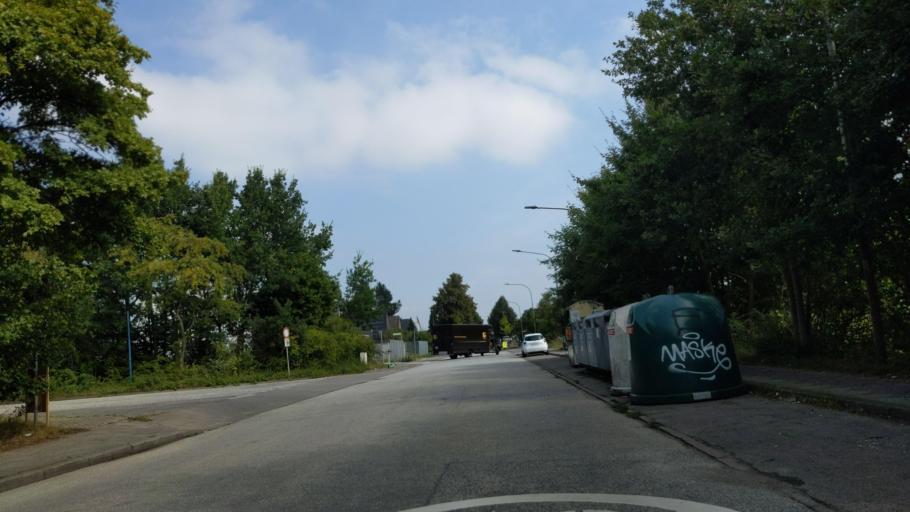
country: DE
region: Schleswig-Holstein
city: Stockelsdorf
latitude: 53.8704
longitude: 10.6226
